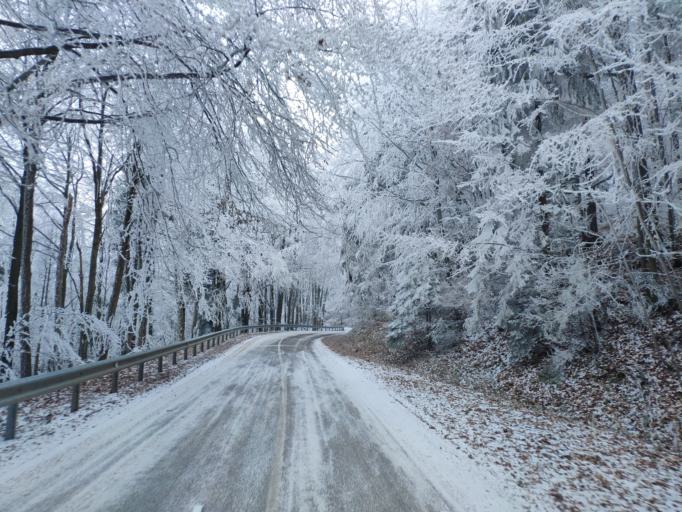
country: SK
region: Kosicky
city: Dobsina
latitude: 48.8092
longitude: 20.4820
